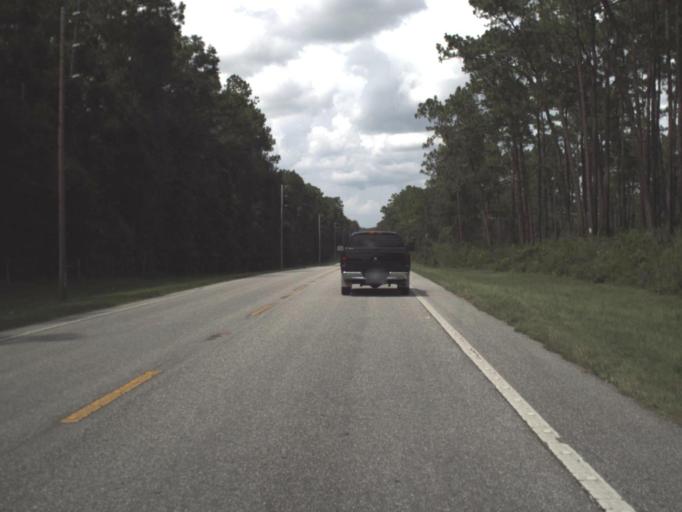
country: US
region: Florida
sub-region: Hernando County
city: North Brooksville
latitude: 28.6454
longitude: -82.3335
